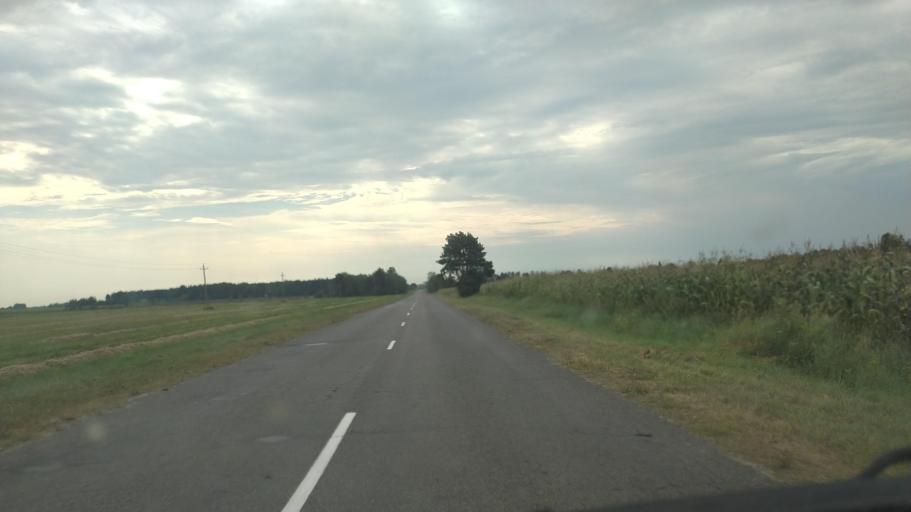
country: BY
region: Brest
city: Byaroza
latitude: 52.5645
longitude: 24.9025
